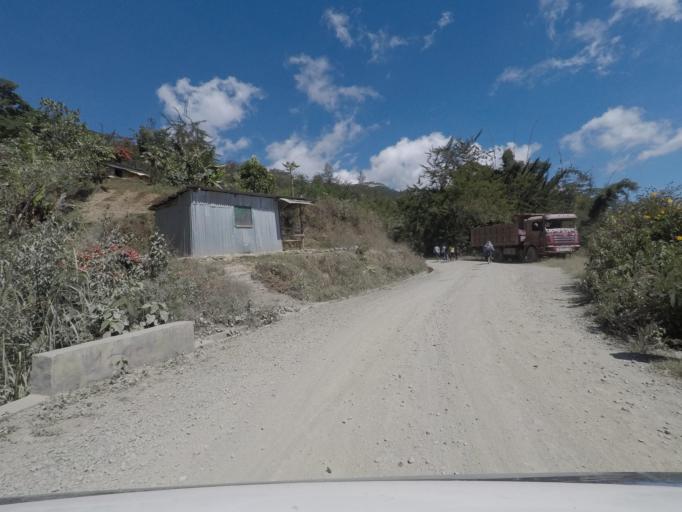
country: TL
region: Ermera
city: Gleno
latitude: -8.7464
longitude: 125.3892
